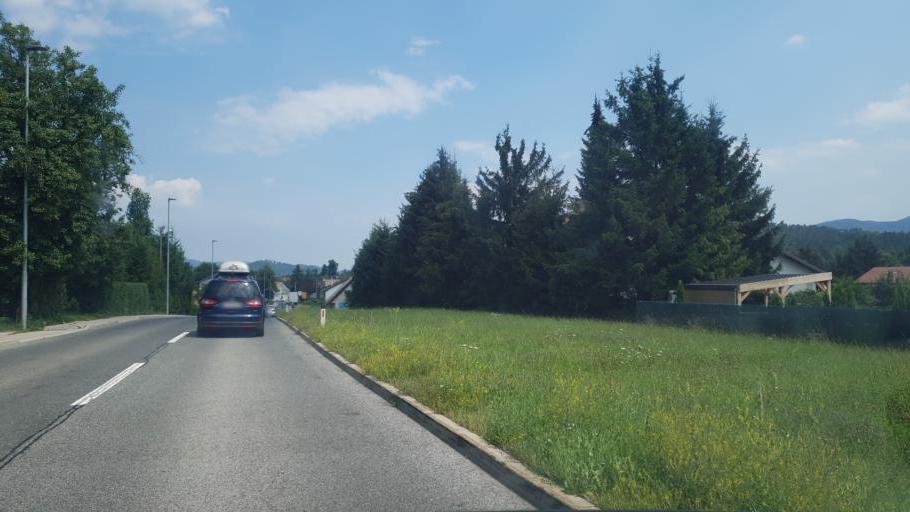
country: SI
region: Postojna
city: Postojna
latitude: 45.7425
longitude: 14.1934
